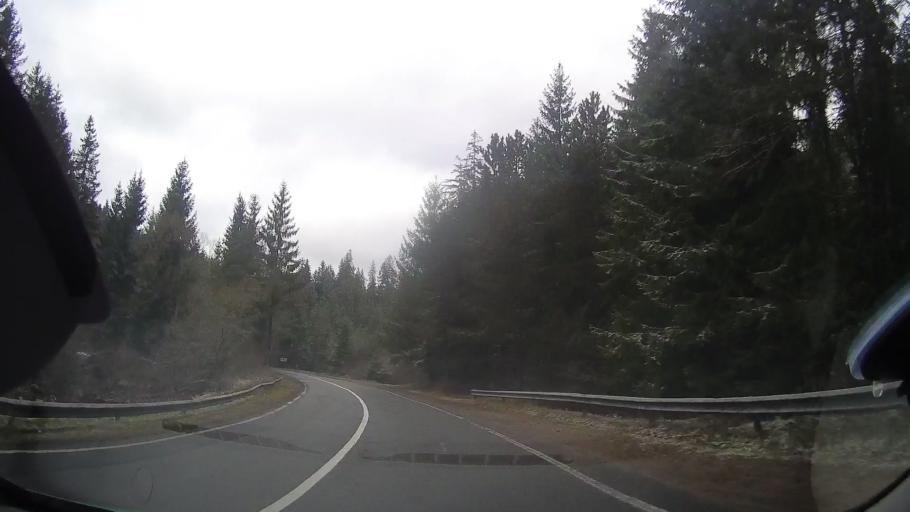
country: RO
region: Cluj
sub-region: Comuna Calatele
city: Calatele
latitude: 46.7467
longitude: 23.0152
